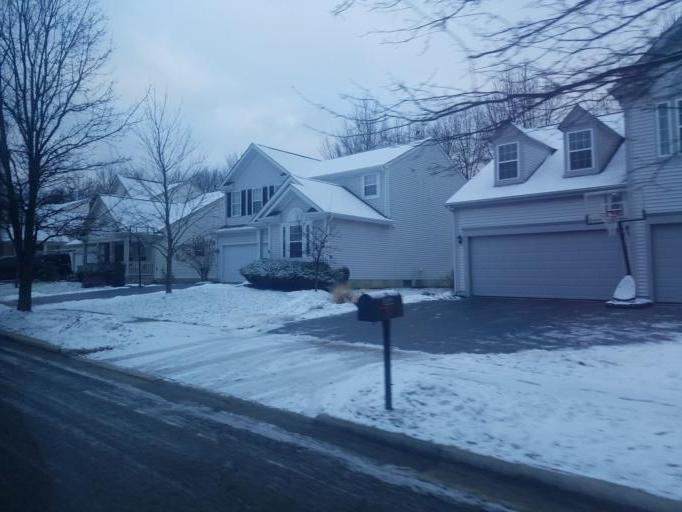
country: US
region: Ohio
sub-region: Franklin County
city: New Albany
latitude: 40.0702
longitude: -82.8524
